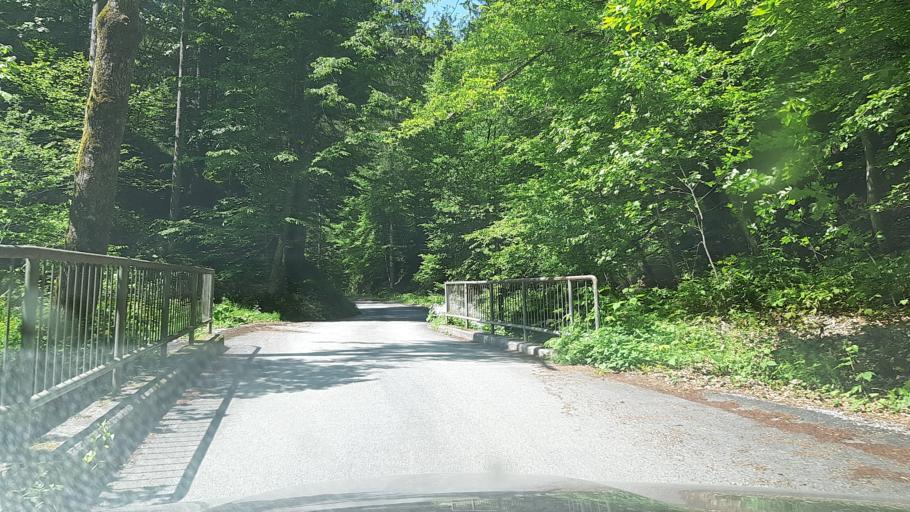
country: SI
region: Skofja Loka
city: Skofja Loka
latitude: 46.1201
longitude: 14.2721
